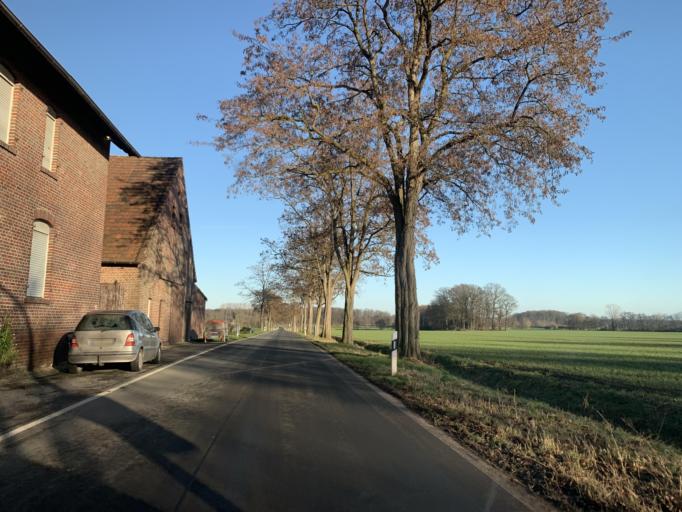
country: DE
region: North Rhine-Westphalia
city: Ludinghausen
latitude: 51.7959
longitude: 7.3761
